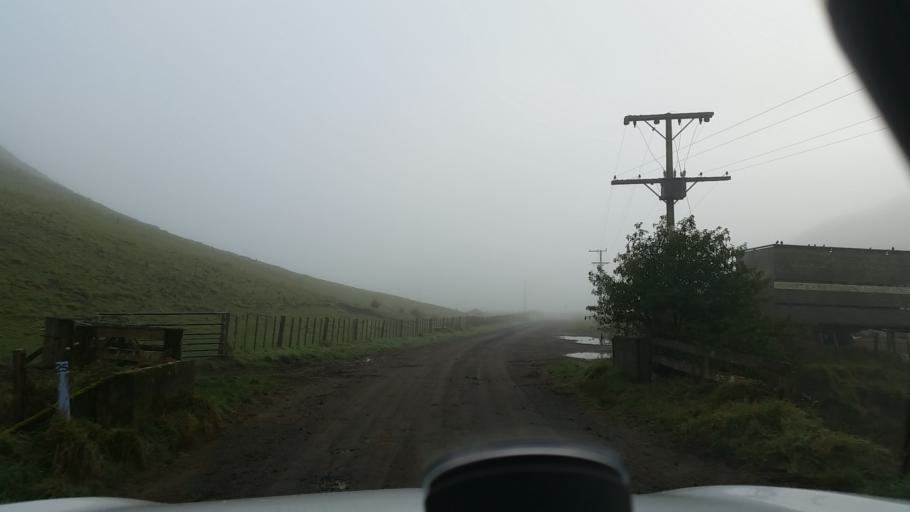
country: NZ
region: Taranaki
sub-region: South Taranaki District
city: Eltham
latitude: -39.4057
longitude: 174.4308
